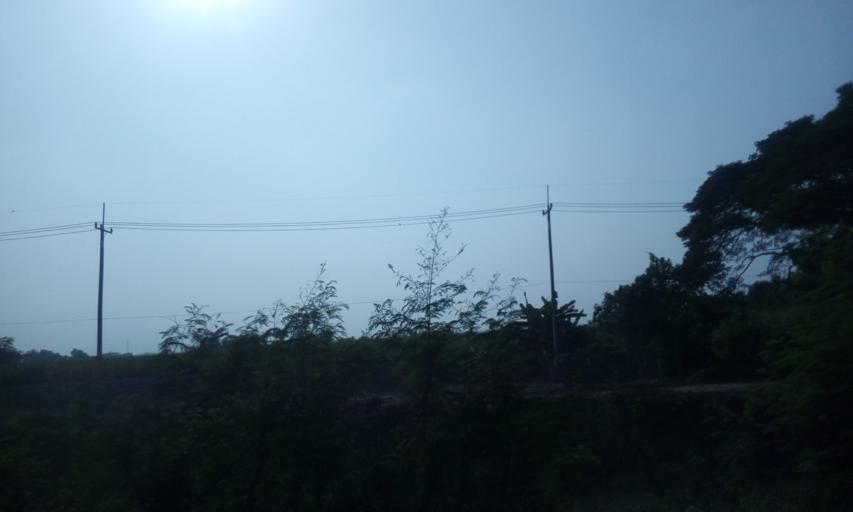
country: TH
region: Sing Buri
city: Phrom Buri
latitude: 14.7491
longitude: 100.4411
